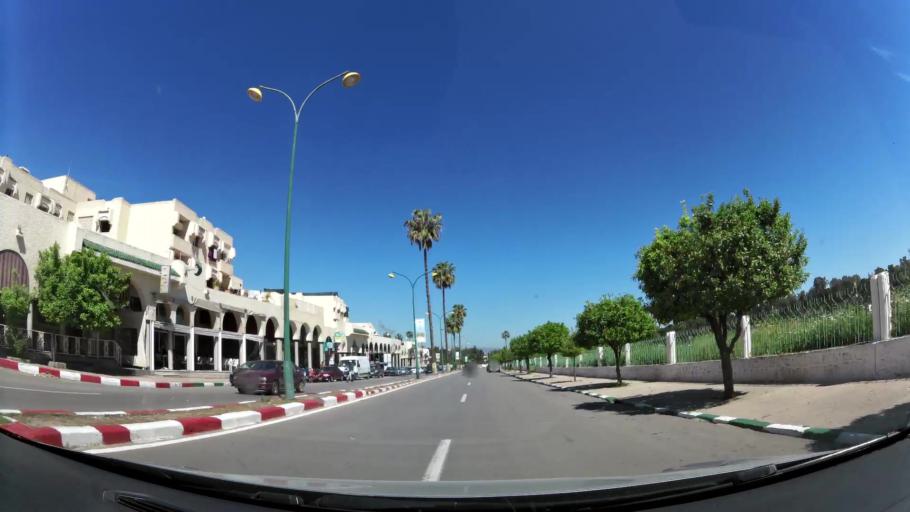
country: MA
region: Meknes-Tafilalet
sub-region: Meknes
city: Meknes
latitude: 33.8938
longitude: -5.5564
